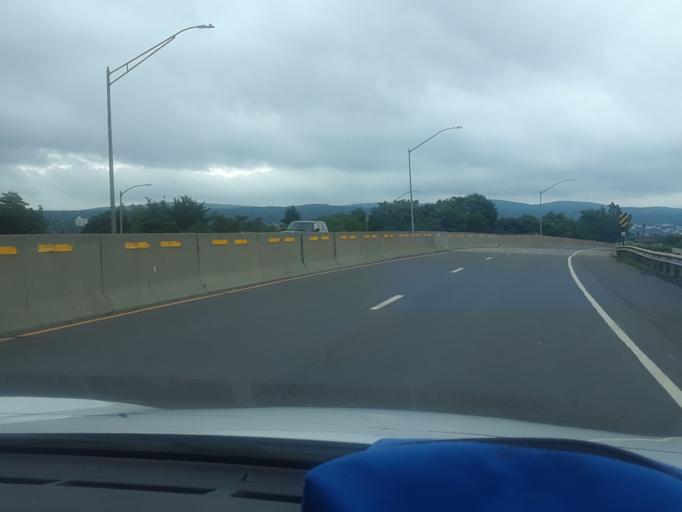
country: US
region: Pennsylvania
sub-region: Lackawanna County
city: Scranton
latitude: 41.4261
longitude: -75.6710
